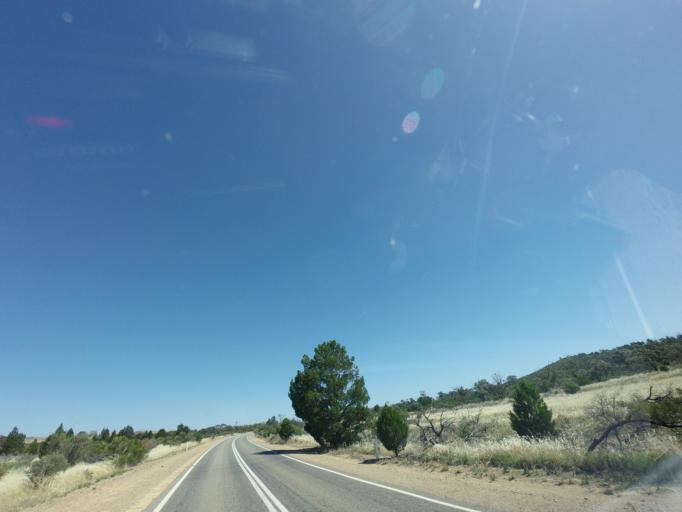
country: AU
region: South Australia
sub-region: Peterborough
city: Peterborough
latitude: -32.9176
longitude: 138.7694
